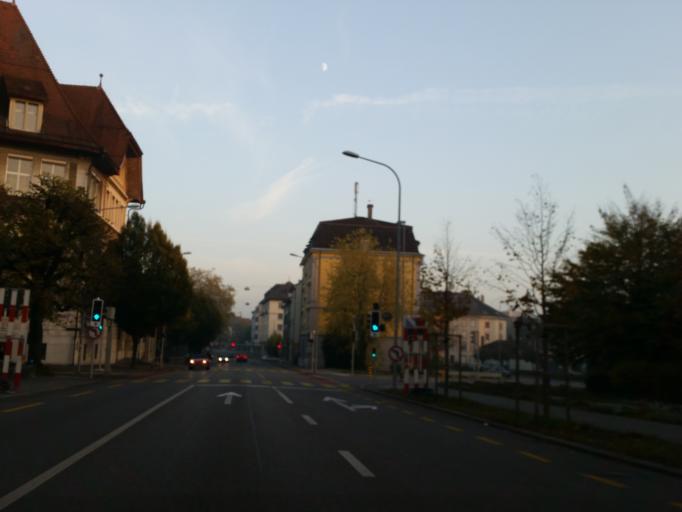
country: CH
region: Solothurn
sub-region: Bezirk Solothurn
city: Solothurn
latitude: 47.2098
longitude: 7.5305
